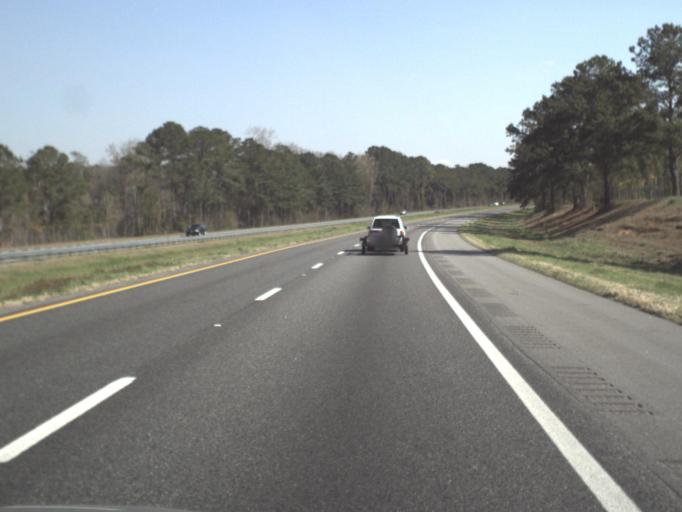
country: US
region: Florida
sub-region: Gadsden County
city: Gretna
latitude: 30.6019
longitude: -84.7302
